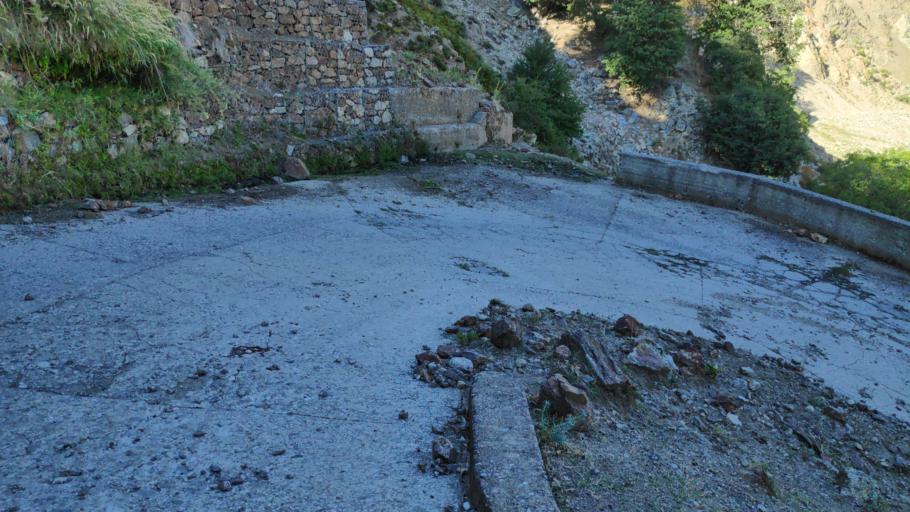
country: IT
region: Calabria
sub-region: Provincia di Reggio Calabria
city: Roccaforte del Greco
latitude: 38.0523
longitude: 15.9278
